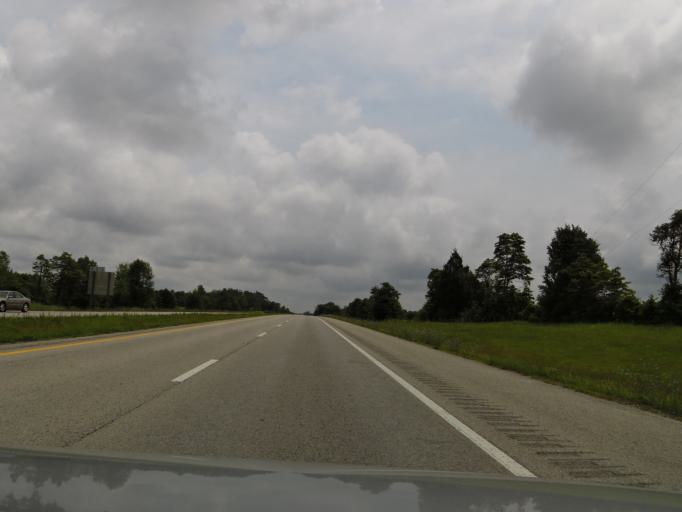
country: US
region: Kentucky
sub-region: Grayson County
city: Leitchfield
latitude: 37.4942
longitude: -86.1889
